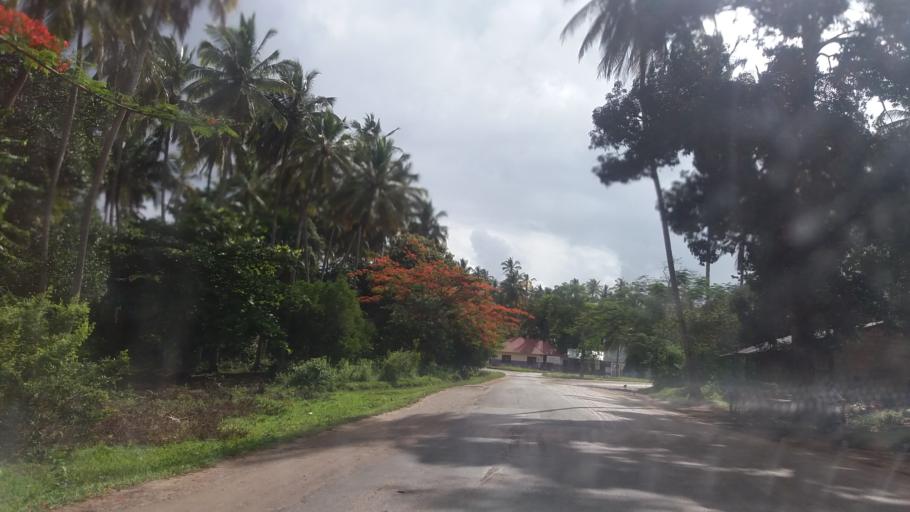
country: TZ
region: Zanzibar Central/South
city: Koani
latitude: -6.2037
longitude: 39.3243
